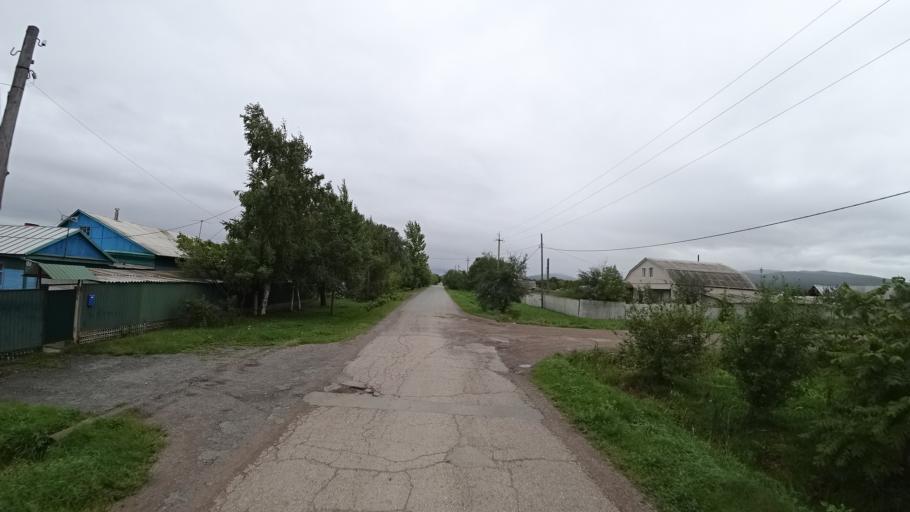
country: RU
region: Primorskiy
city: Chernigovka
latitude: 44.3324
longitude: 132.5918
